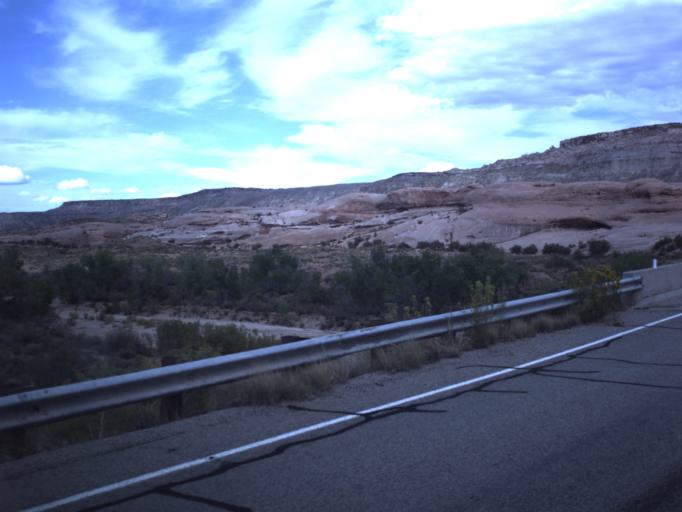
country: US
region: Utah
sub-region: San Juan County
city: Blanding
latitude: 37.3002
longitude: -109.4580
